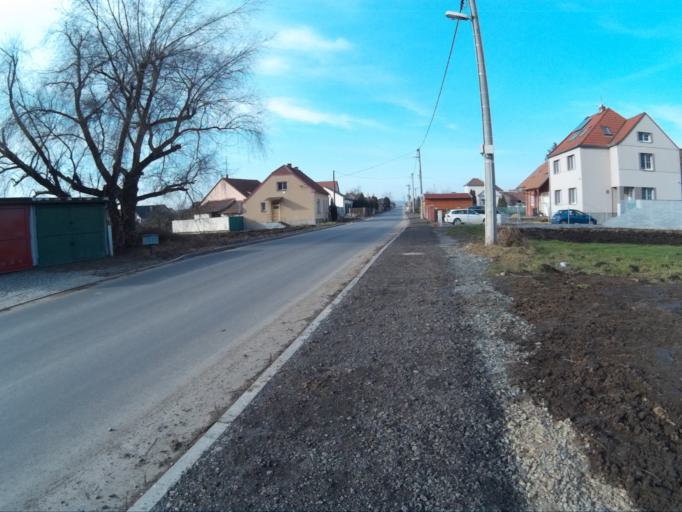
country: CZ
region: South Moravian
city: Troubsko
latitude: 49.1638
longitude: 16.5255
